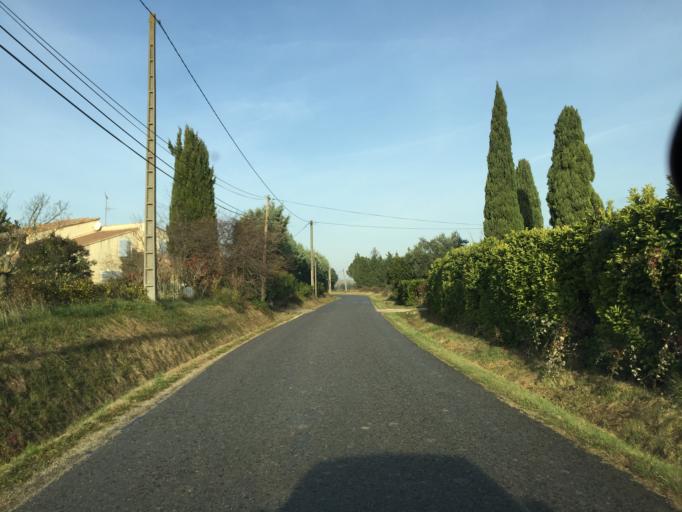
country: FR
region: Provence-Alpes-Cote d'Azur
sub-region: Departement du Vaucluse
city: Orange
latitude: 44.1402
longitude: 4.7890
